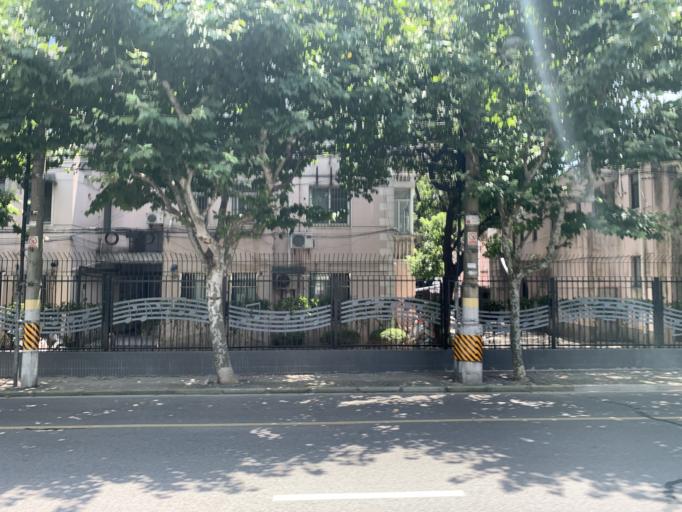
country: CN
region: Shanghai Shi
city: Pudong
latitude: 31.2404
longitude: 121.5254
